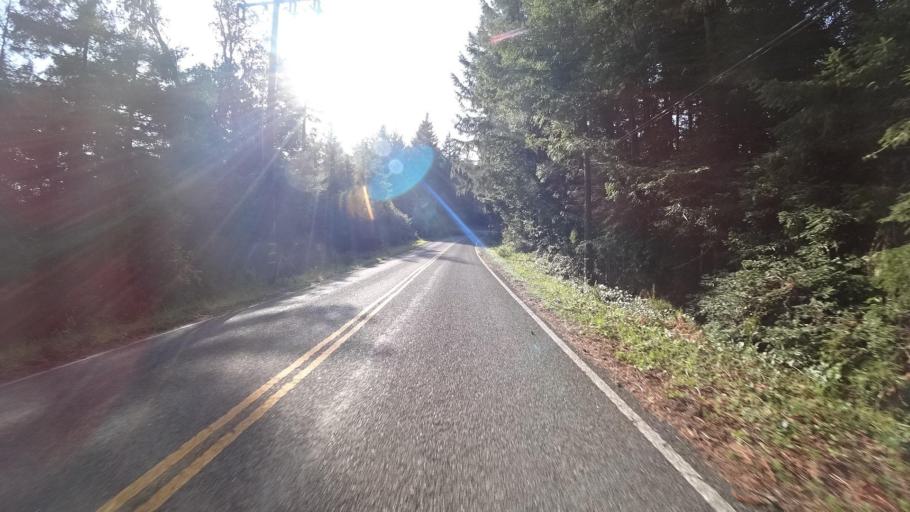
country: US
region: California
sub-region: Humboldt County
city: Bayside
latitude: 40.7487
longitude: -123.9760
